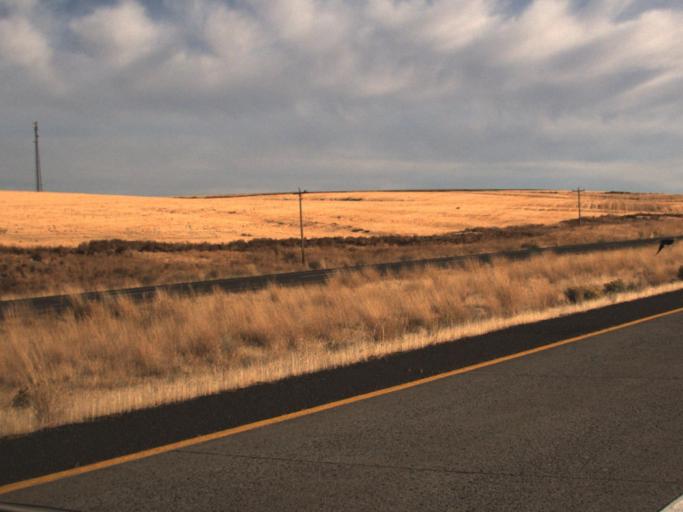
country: US
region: Washington
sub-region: Franklin County
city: Connell
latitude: 46.7702
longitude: -118.7791
